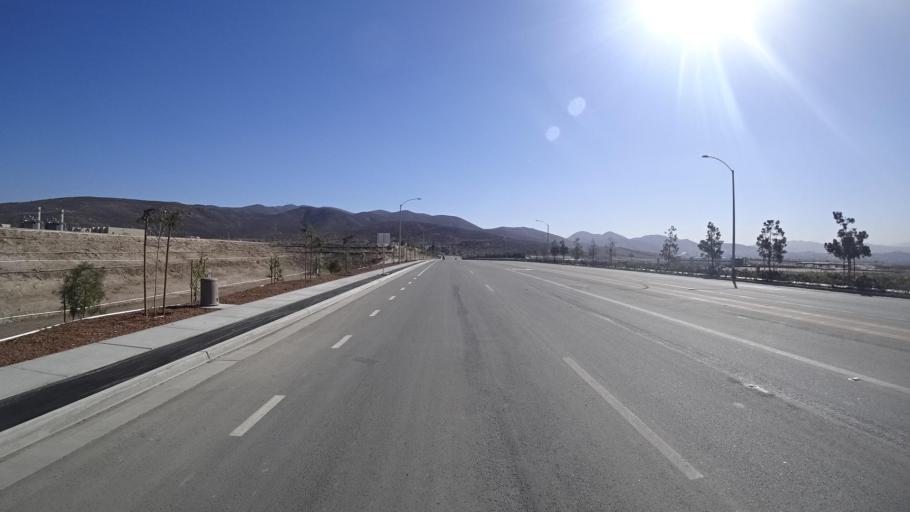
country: MX
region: Baja California
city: Tijuana
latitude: 32.5674
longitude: -116.9186
